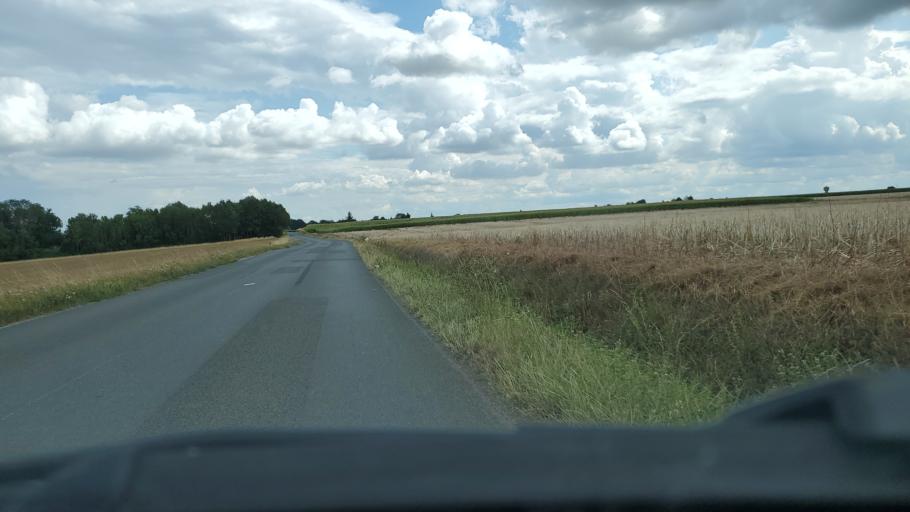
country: FR
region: Ile-de-France
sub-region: Departement de Seine-et-Marne
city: Mouroux
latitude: 48.8393
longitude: 3.0310
